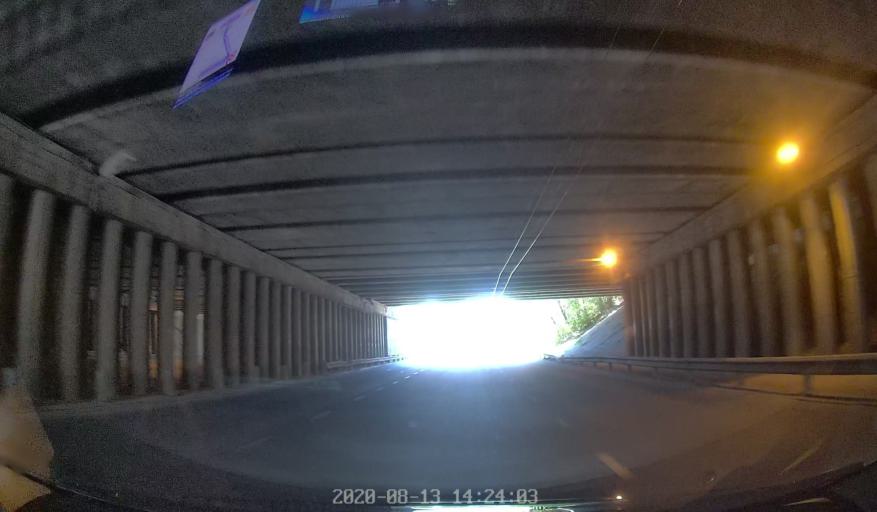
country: NG
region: Niger
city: Lemu
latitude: 9.2933
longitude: 6.1373
